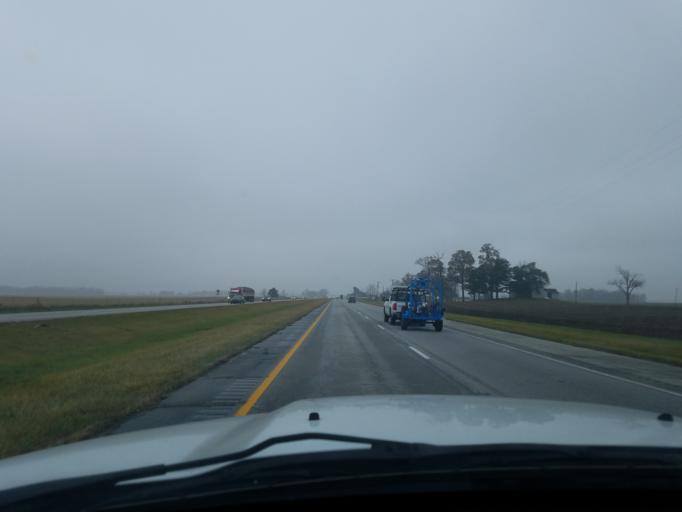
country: US
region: Indiana
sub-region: Tipton County
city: Tipton
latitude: 40.2572
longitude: -86.1273
